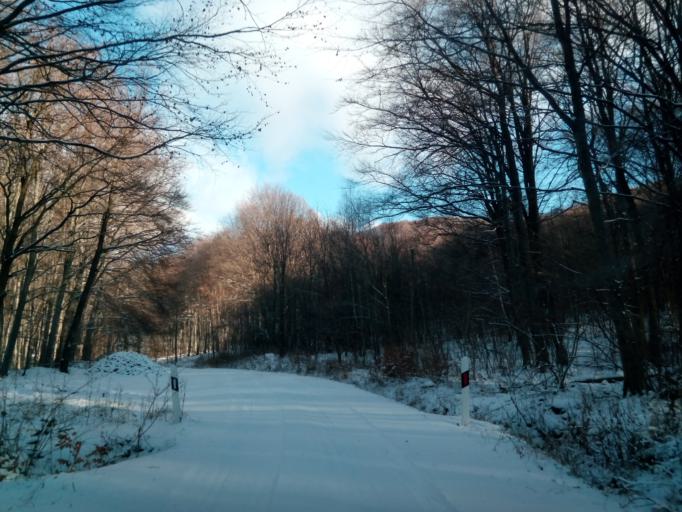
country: HU
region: Borsod-Abauj-Zemplen
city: Gonc
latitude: 48.5708
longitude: 21.4381
